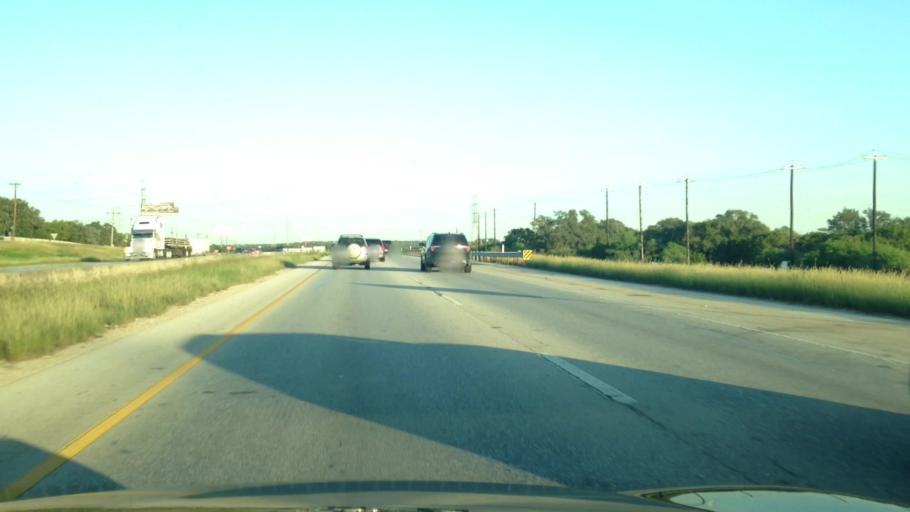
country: US
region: Texas
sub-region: Bexar County
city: Hollywood Park
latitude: 29.6018
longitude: -98.4405
